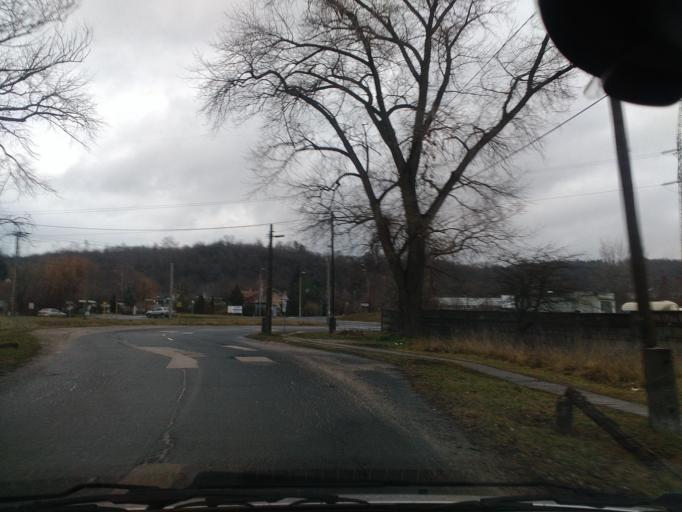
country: HU
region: Komarom-Esztergom
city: Dorog
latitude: 47.7111
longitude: 18.7334
